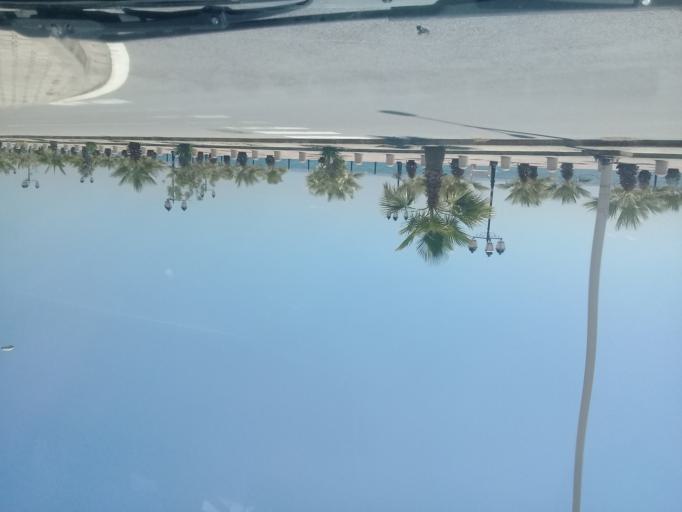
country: TN
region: Tunis
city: La Goulette
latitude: 36.8415
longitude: 10.2810
